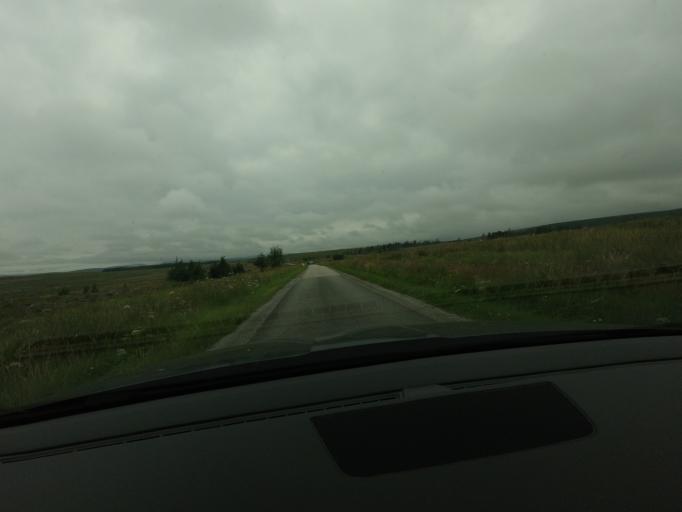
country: GB
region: Scotland
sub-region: Highland
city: Evanton
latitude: 58.1593
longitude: -4.4916
